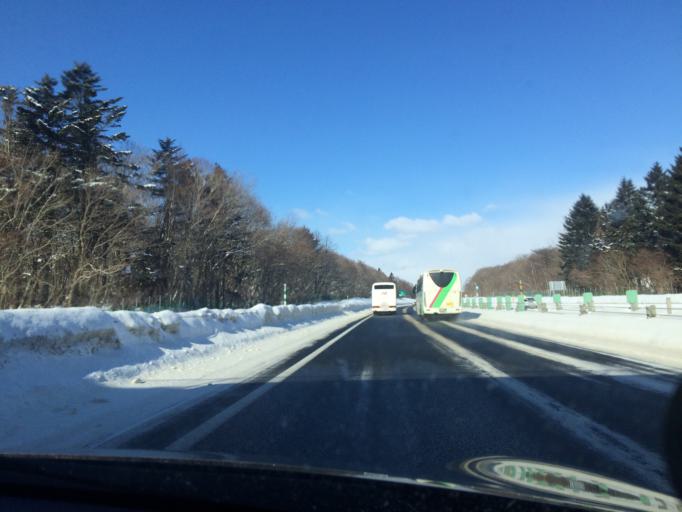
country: JP
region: Hokkaido
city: Chitose
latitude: 42.8571
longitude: 141.5620
